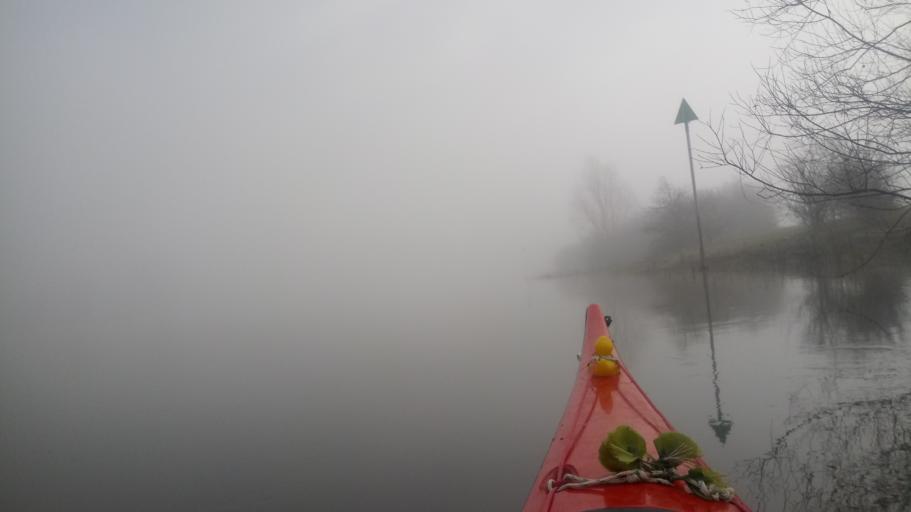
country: NL
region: Gelderland
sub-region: Gemeente Zutphen
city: Zutphen
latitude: 52.1137
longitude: 6.1986
